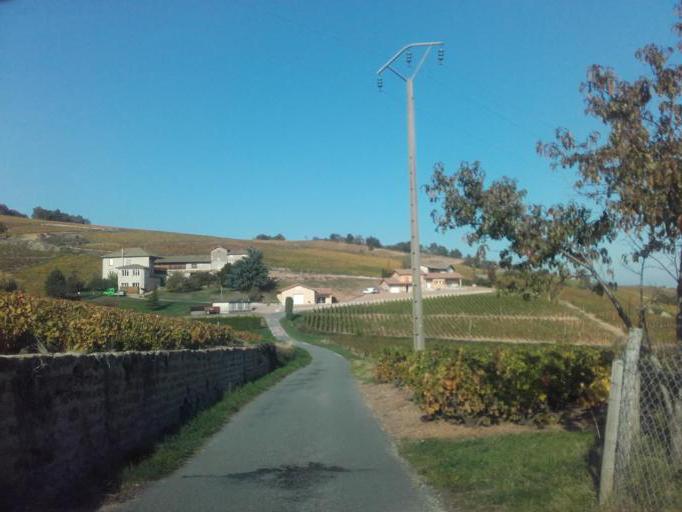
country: FR
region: Rhone-Alpes
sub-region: Departement du Rhone
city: Fleurie
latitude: 46.2041
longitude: 4.7027
